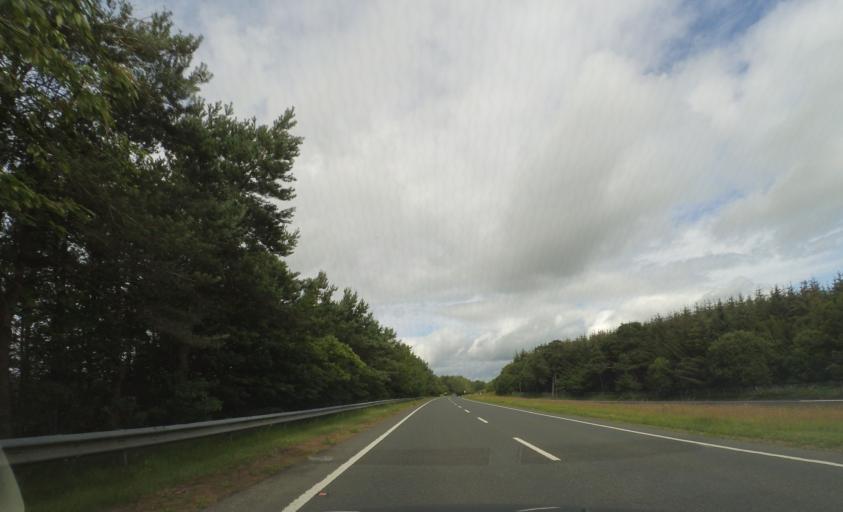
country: GB
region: Scotland
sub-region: The Scottish Borders
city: Hawick
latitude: 55.4755
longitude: -2.8110
